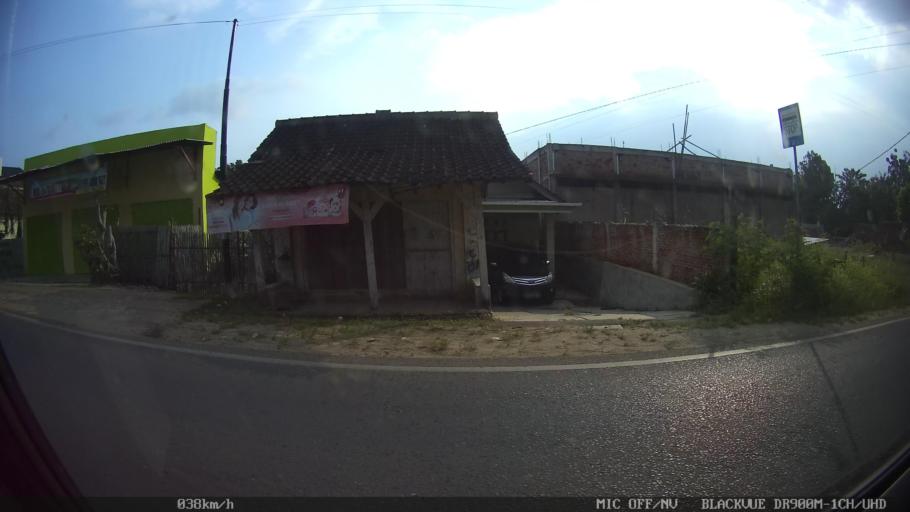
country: ID
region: Lampung
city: Kedaton
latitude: -5.3865
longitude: 105.2022
